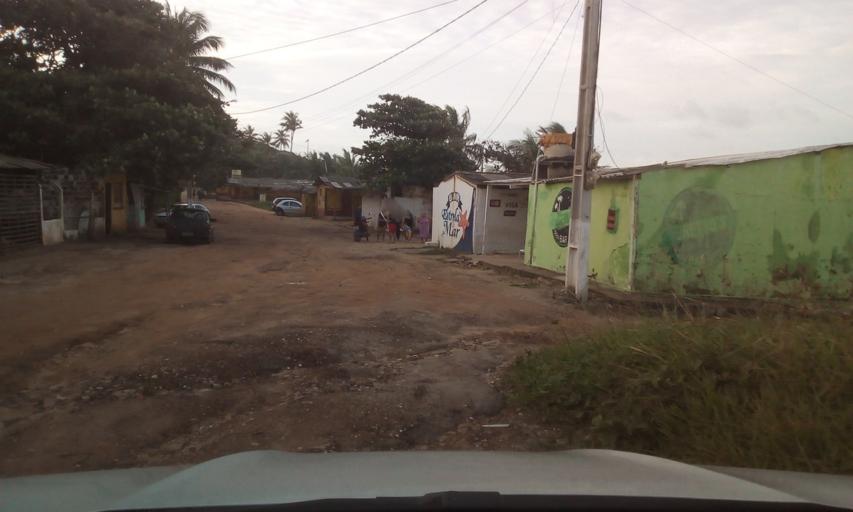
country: BR
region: Paraiba
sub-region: Conde
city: Conde
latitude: -7.2176
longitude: -34.8046
